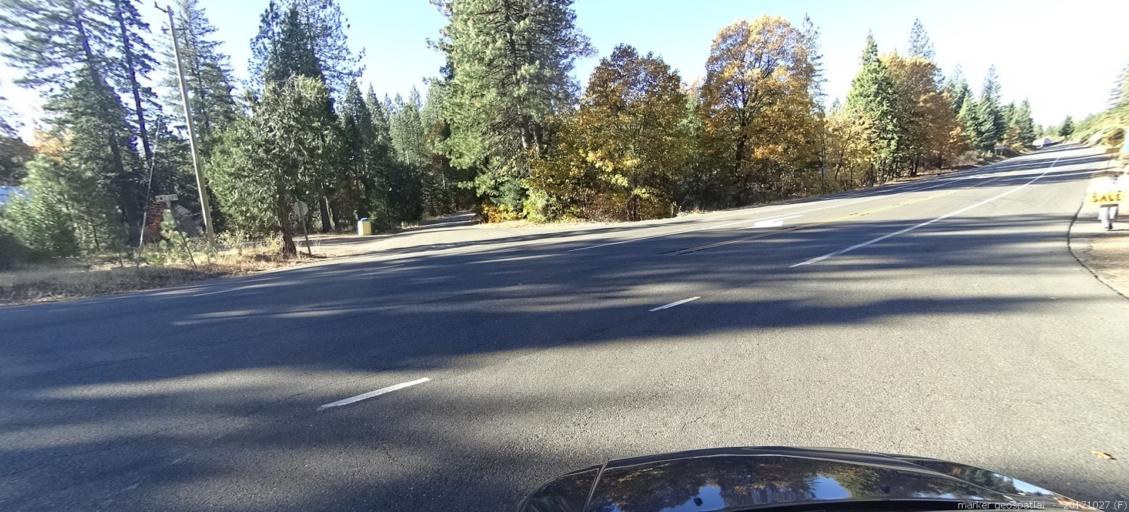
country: US
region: California
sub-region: Shasta County
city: Burney
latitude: 40.8657
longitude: -121.9074
